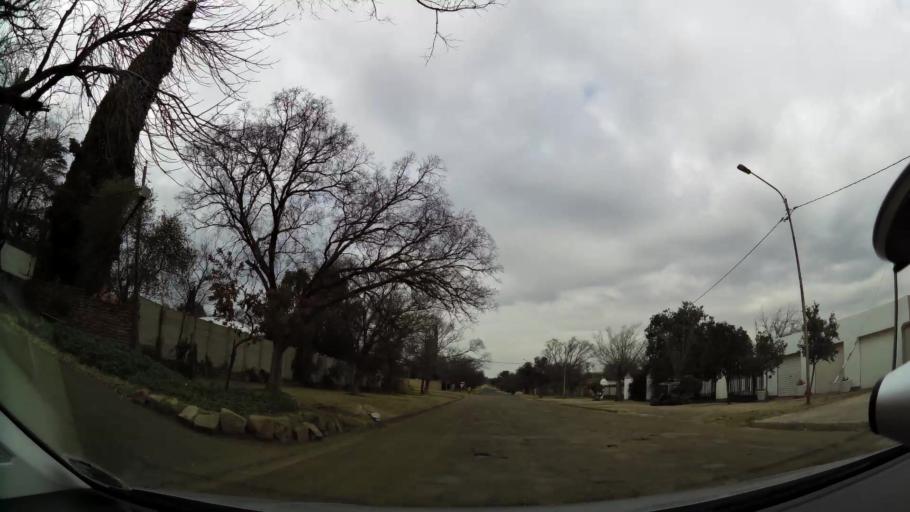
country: ZA
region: Orange Free State
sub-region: Fezile Dabi District Municipality
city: Kroonstad
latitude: -27.6786
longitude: 27.2439
